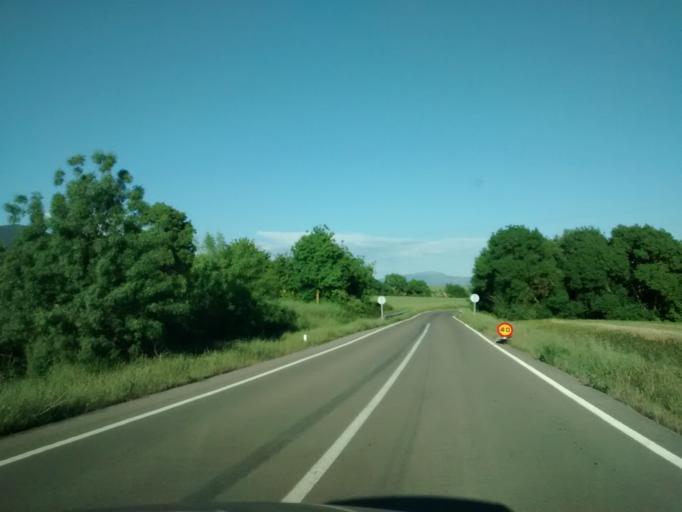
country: ES
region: Aragon
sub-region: Provincia de Huesca
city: Jaca
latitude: 42.5802
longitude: -0.5746
